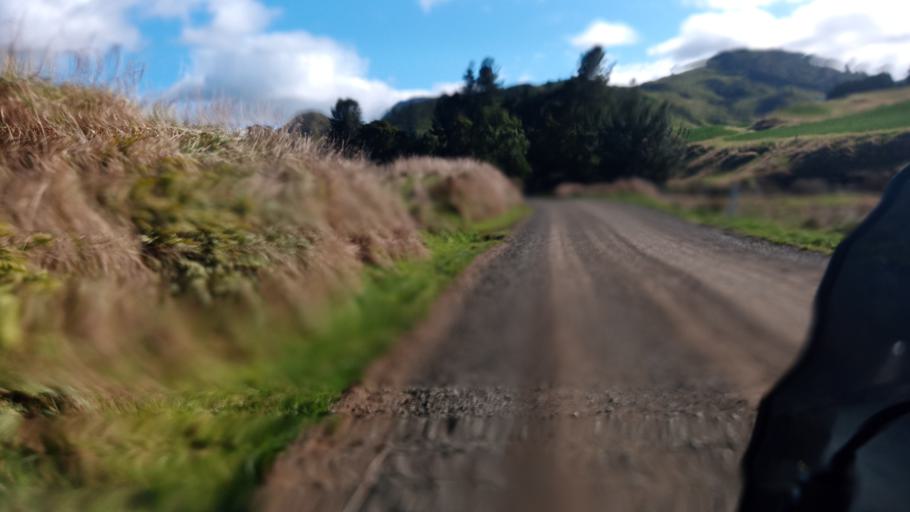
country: NZ
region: Bay of Plenty
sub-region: Opotiki District
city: Opotiki
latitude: -38.4653
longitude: 177.4270
